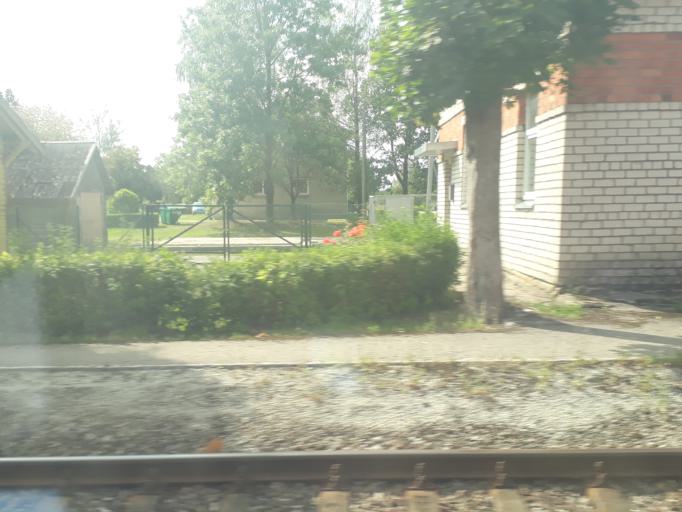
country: EE
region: Laeaene-Virumaa
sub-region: Tamsalu vald
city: Tamsalu
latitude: 59.1603
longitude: 26.1109
